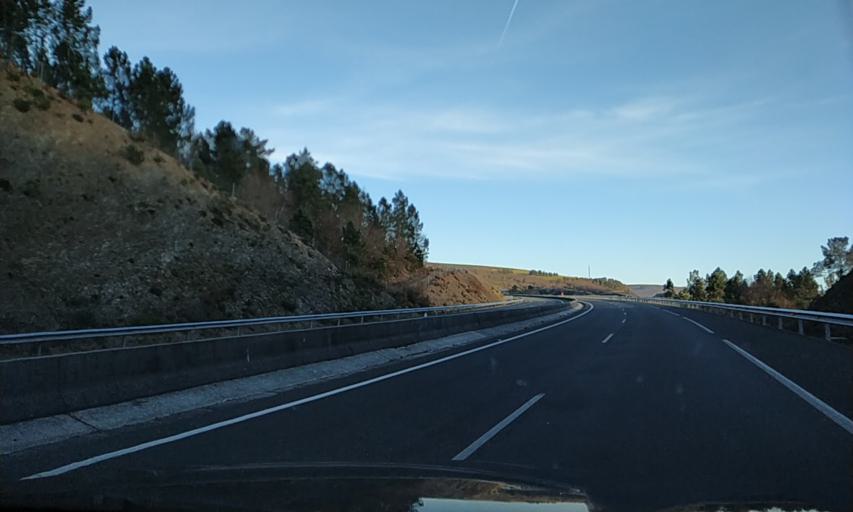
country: ES
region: Galicia
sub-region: Provincia de Pontevedra
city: Lalin
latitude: 42.6033
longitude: -8.0983
